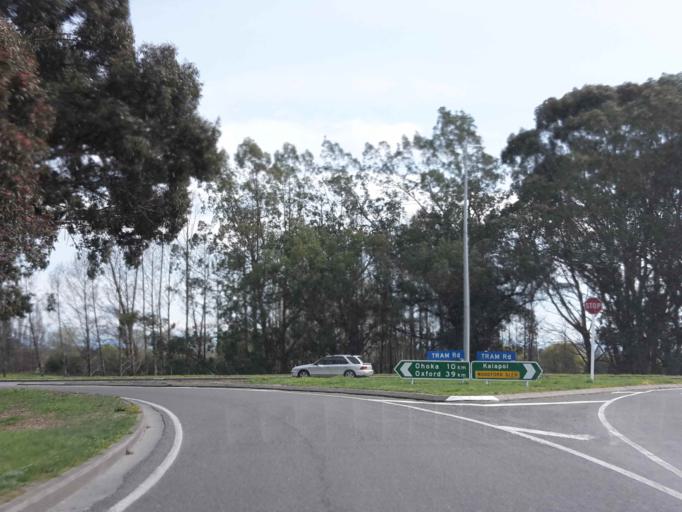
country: NZ
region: Canterbury
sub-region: Waimakariri District
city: Kaiapoi
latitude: -43.4085
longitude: 172.6441
